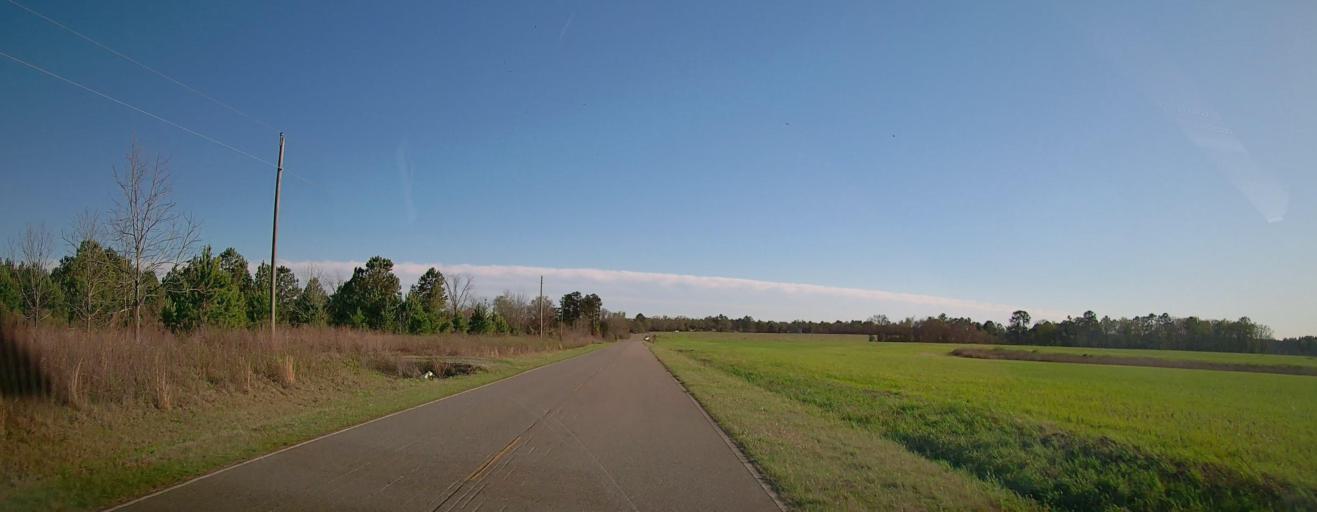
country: US
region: Georgia
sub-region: Pulaski County
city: Hawkinsville
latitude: 32.2504
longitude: -83.5878
